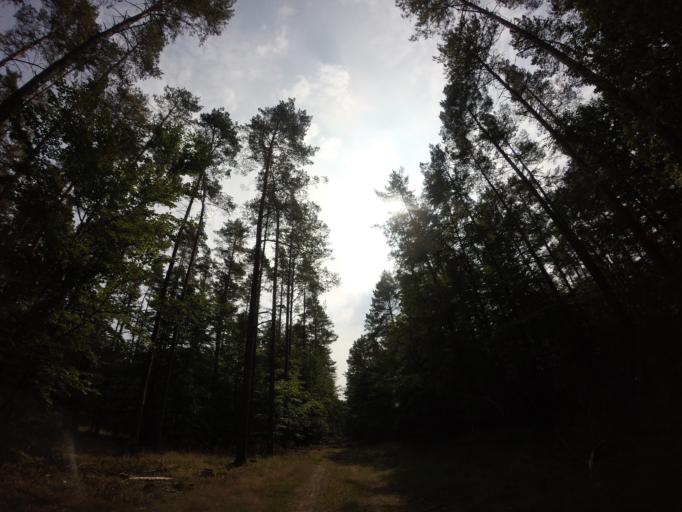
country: PL
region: West Pomeranian Voivodeship
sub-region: Powiat drawski
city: Drawsko Pomorskie
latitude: 53.4590
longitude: 15.7187
